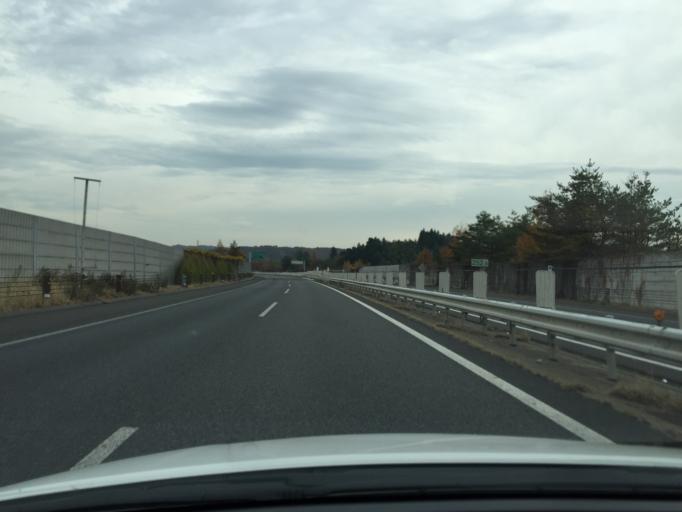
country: JP
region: Fukushima
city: Fukushima-shi
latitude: 37.7210
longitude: 140.4307
